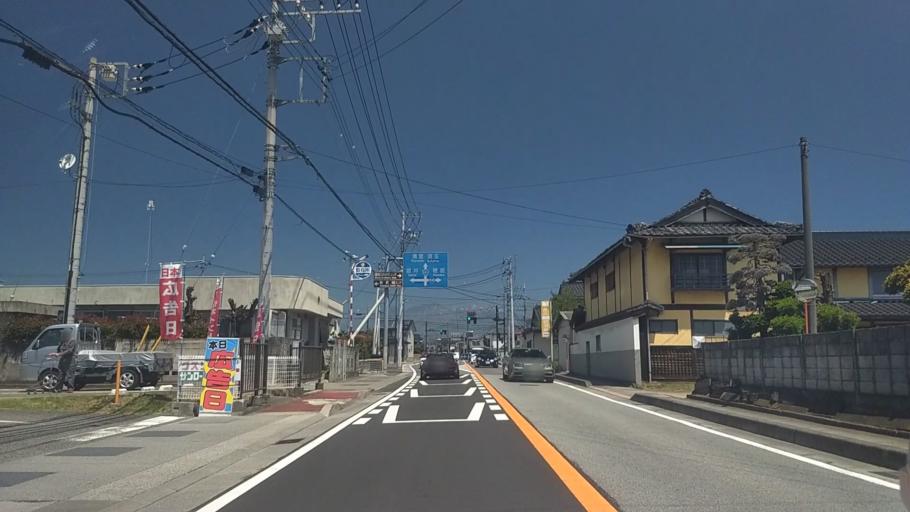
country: JP
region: Yamanashi
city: Nirasaki
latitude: 35.7279
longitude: 138.4490
